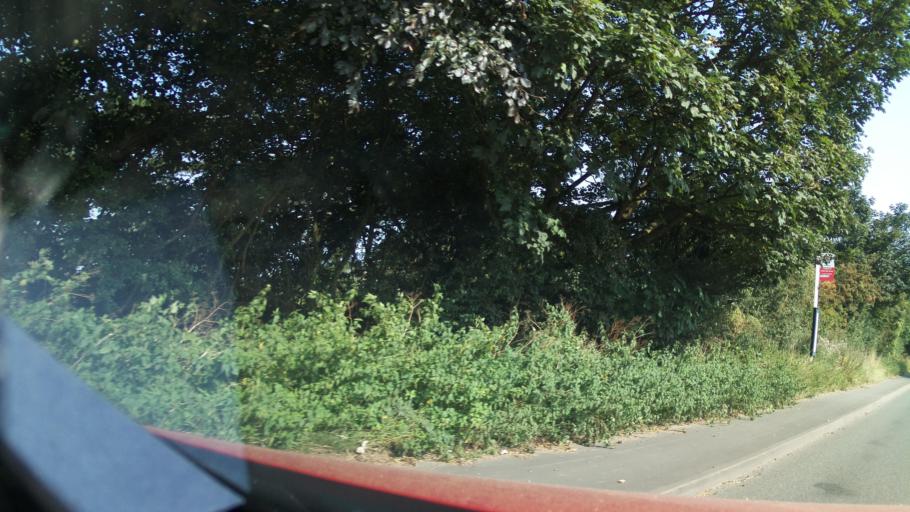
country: GB
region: England
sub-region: Walsall
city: Brownhills
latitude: 52.6379
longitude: -1.9132
